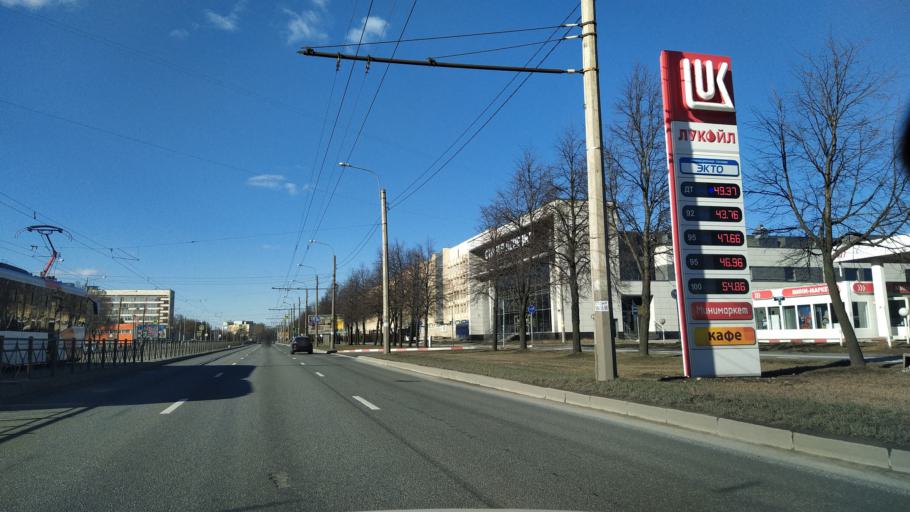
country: RU
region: St.-Petersburg
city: Kupchino
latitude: 59.8893
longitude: 30.3619
